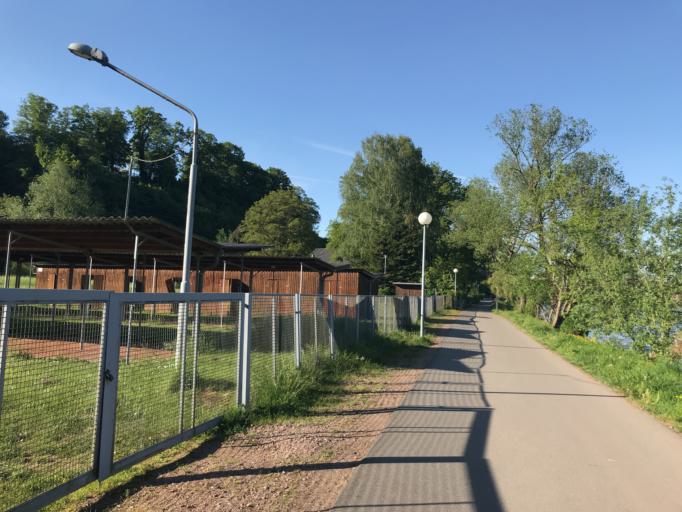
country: DE
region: Saxony
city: Rochlitz
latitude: 51.0421
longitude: 12.7896
